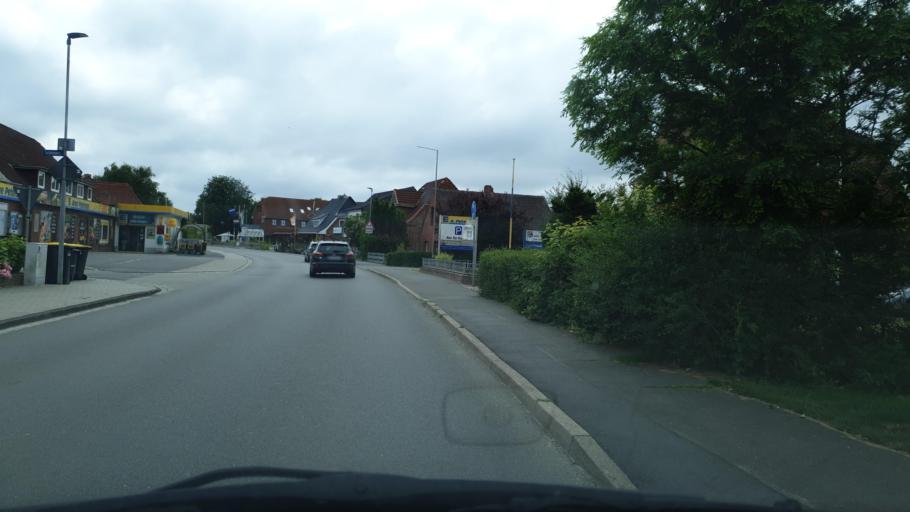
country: DE
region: Schleswig-Holstein
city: Friedrichskoog
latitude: 54.0076
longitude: 8.8824
